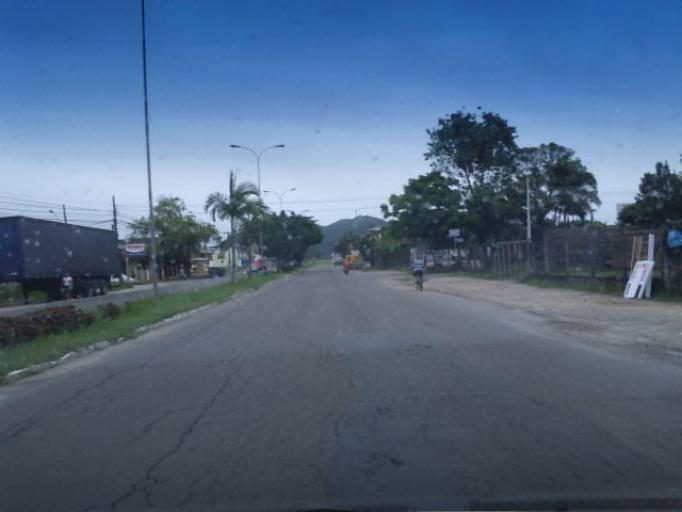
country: BR
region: Santa Catarina
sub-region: Itajai
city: Itajai
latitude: -26.8993
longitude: -48.7026
